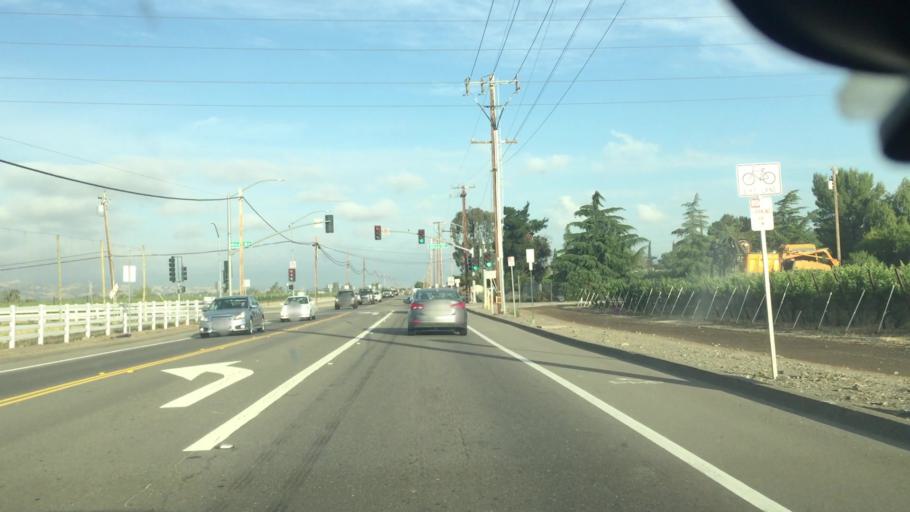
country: US
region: California
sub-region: Alameda County
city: Livermore
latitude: 37.6652
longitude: -121.7321
